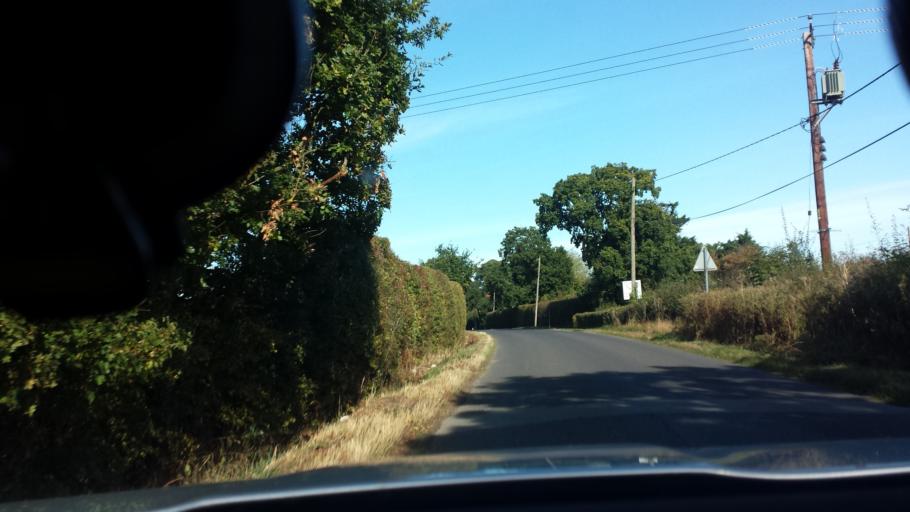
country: GB
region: England
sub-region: Kent
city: Staplehurst
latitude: 51.1956
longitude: 0.5541
